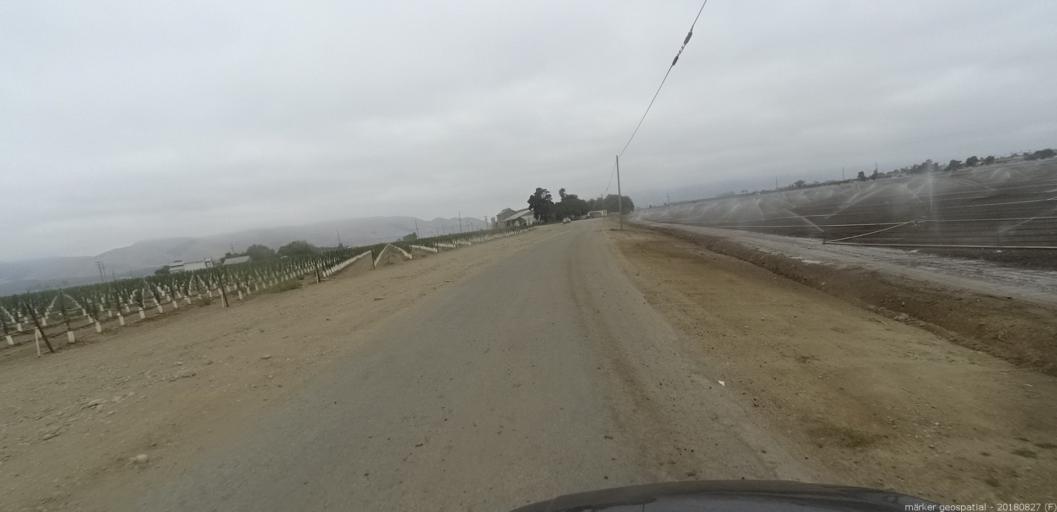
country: US
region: California
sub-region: Monterey County
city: Greenfield
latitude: 36.3105
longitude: -121.2251
